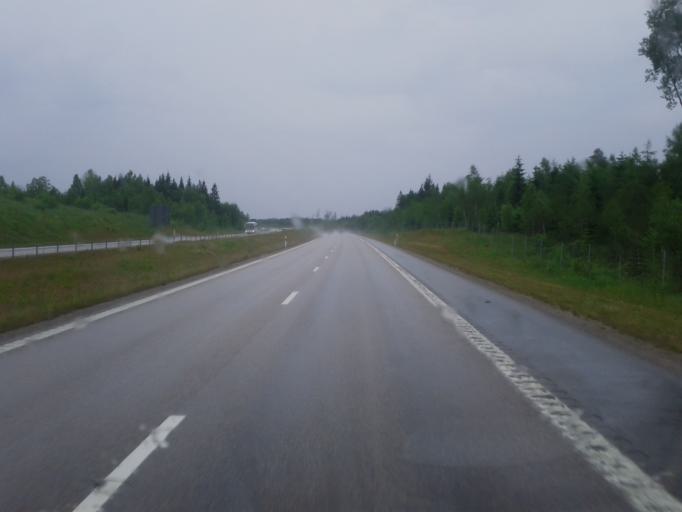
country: SE
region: Uppsala
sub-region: Tierps Kommun
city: Tierp
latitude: 60.3721
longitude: 17.4812
